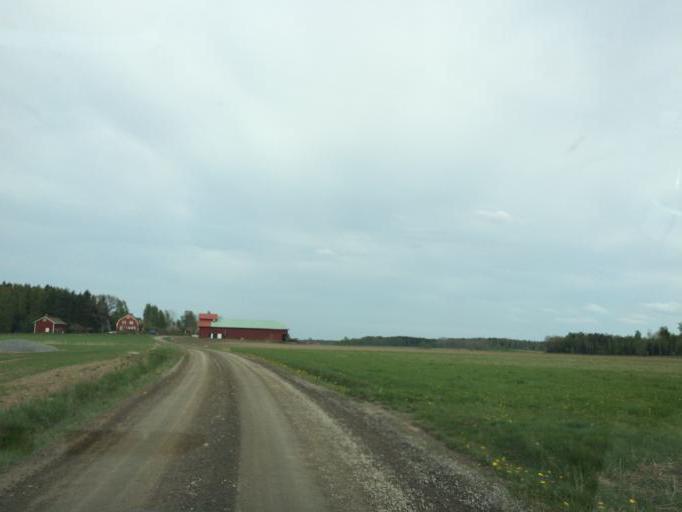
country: SE
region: Vaestmanland
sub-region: Kopings Kommun
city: Koping
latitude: 59.6086
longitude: 16.0708
